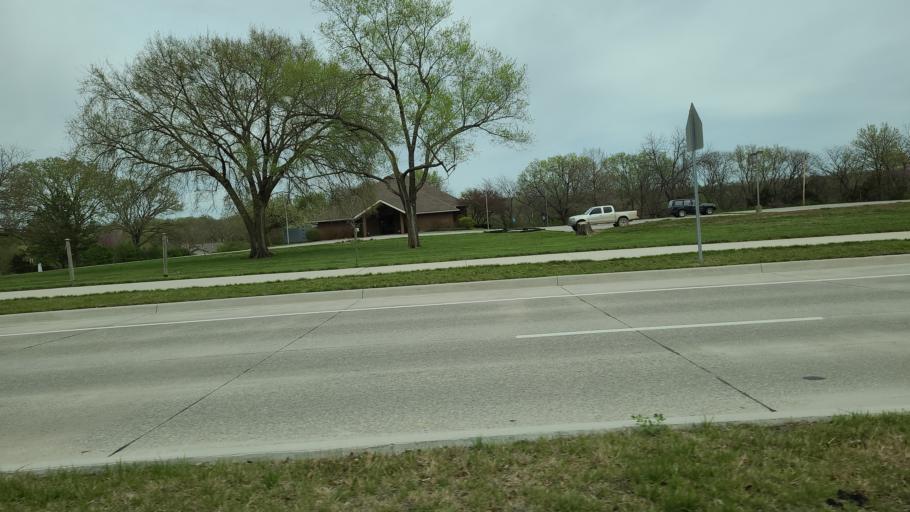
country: US
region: Kansas
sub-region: Douglas County
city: Lawrence
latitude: 38.9636
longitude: -95.2790
